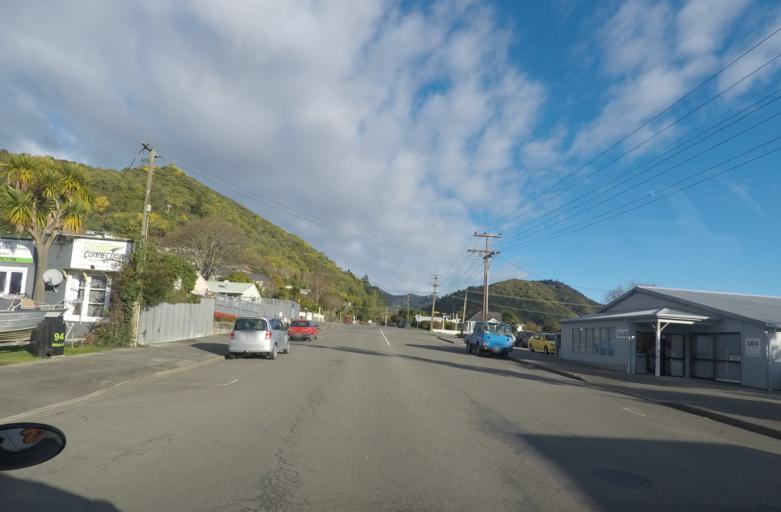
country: NZ
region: Marlborough
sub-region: Marlborough District
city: Picton
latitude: -41.2923
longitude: 174.0078
